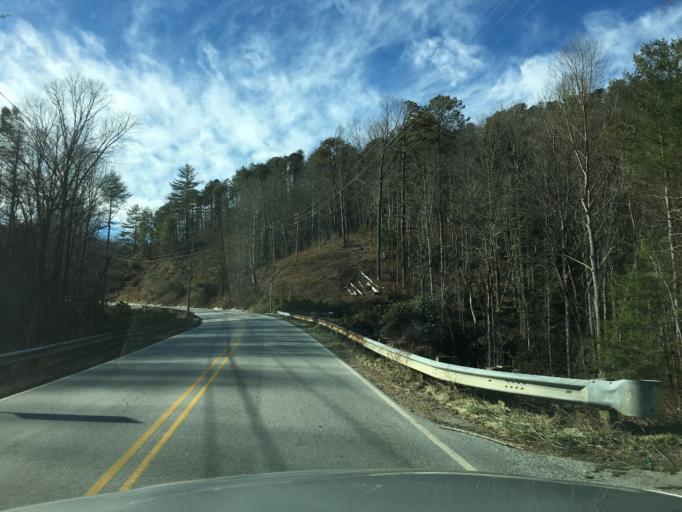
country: US
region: North Carolina
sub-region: Transylvania County
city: Brevard
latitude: 35.1377
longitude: -82.8559
